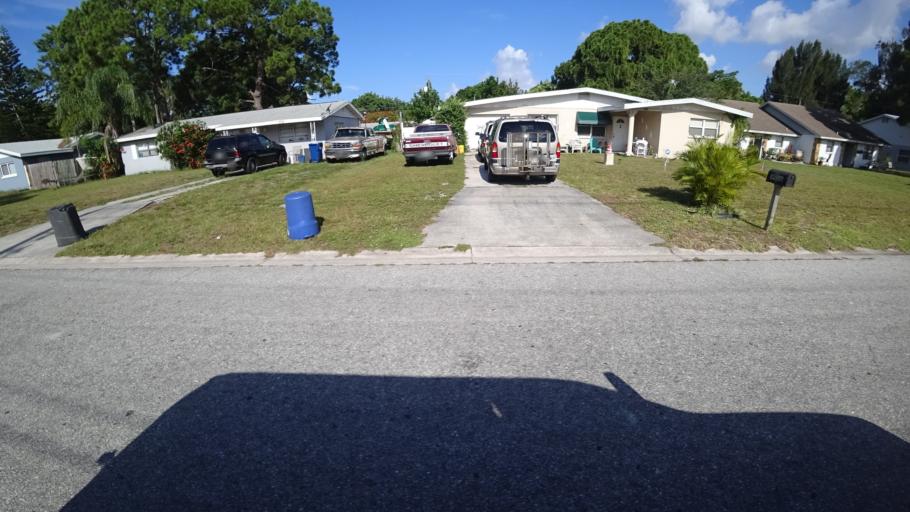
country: US
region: Florida
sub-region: Manatee County
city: South Bradenton
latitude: 27.4658
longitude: -82.5855
